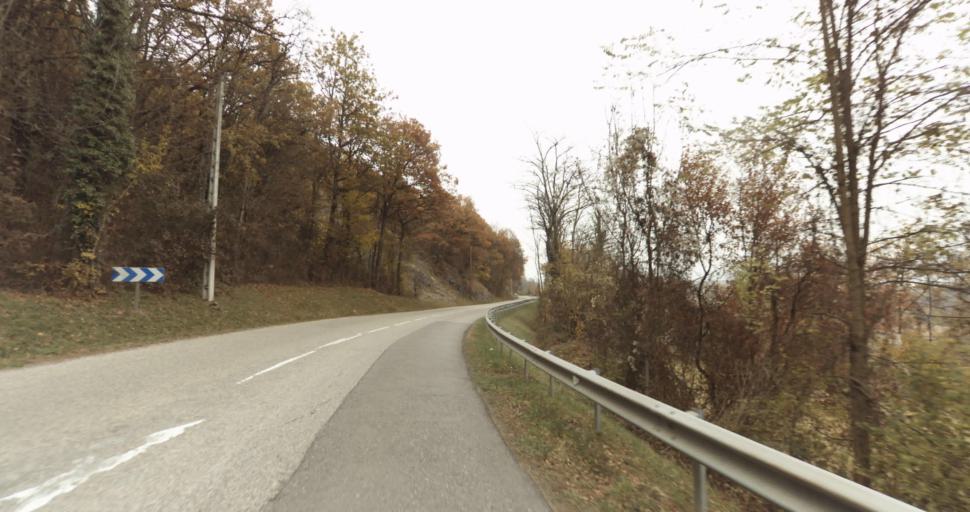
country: FR
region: Rhone-Alpes
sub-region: Departement de la Haute-Savoie
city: Lovagny
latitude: 45.9095
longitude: 6.0470
